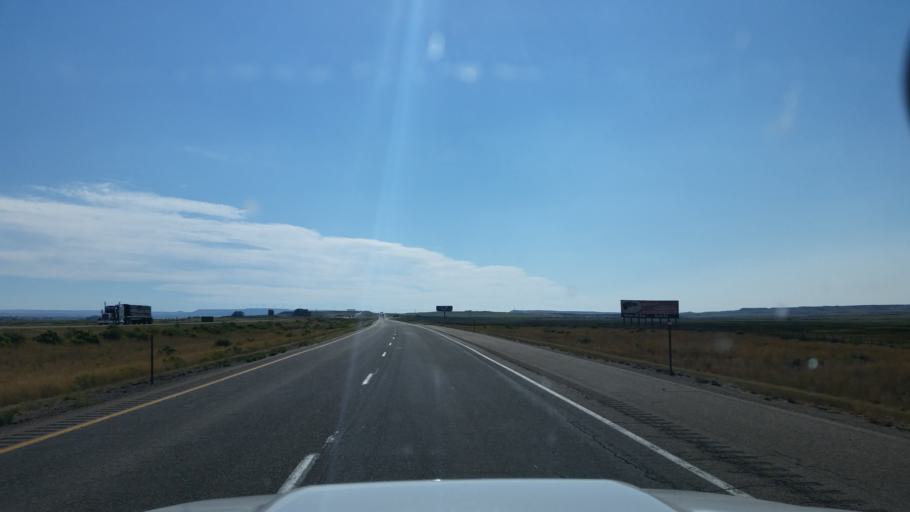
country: US
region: Wyoming
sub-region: Uinta County
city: Lyman
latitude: 41.3625
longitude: -110.3208
